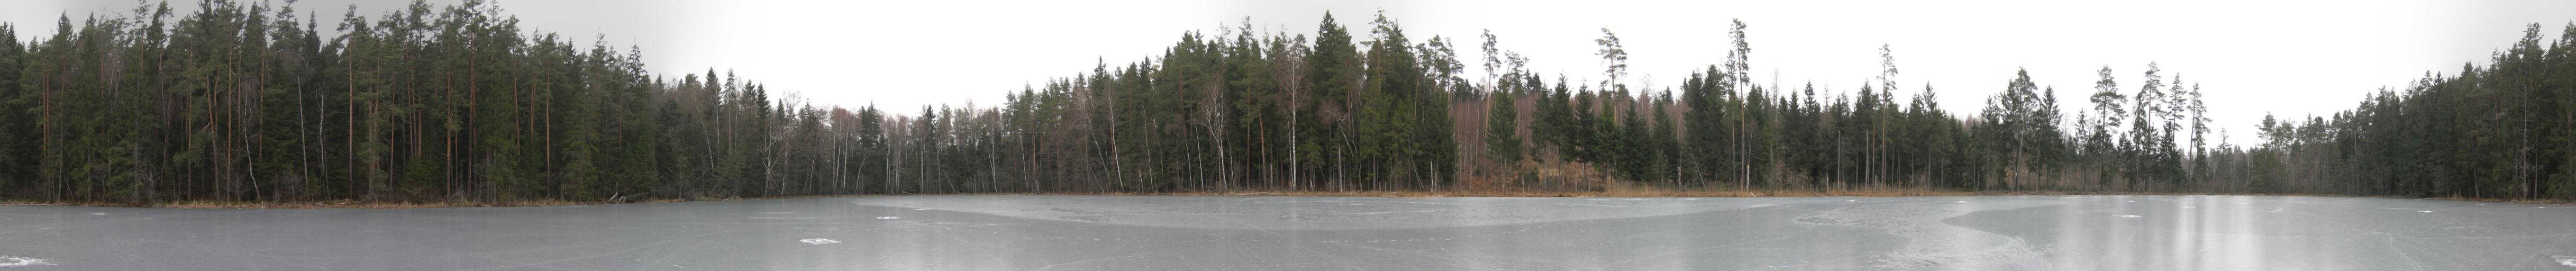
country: LT
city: Zarasai
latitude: 55.6809
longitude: 26.0124
